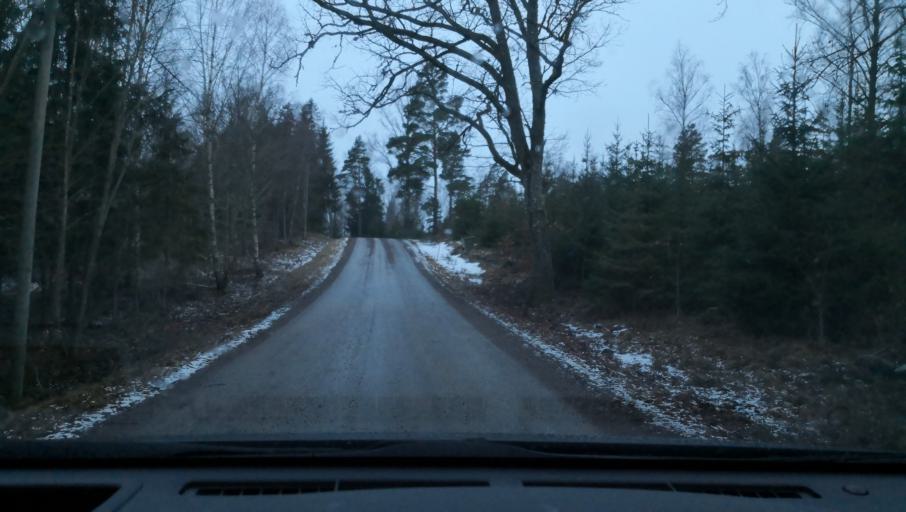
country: SE
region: Soedermanland
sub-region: Eskilstuna Kommun
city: Arla
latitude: 59.4502
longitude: 16.7874
